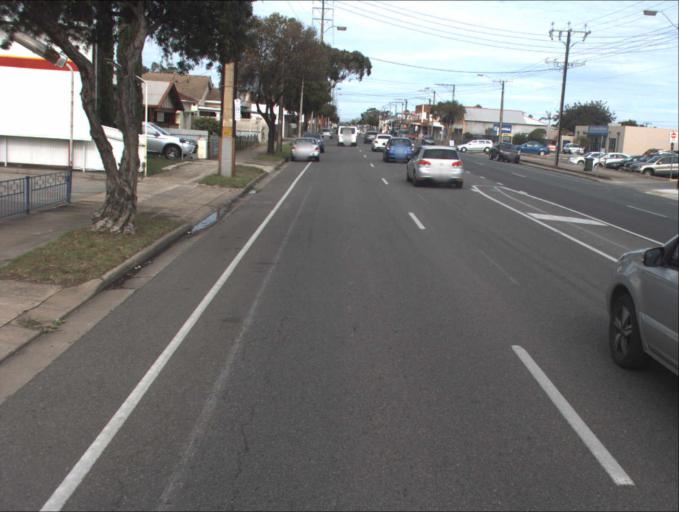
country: AU
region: South Australia
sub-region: Port Adelaide Enfield
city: Cheltenham
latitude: -34.8677
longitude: 138.5120
